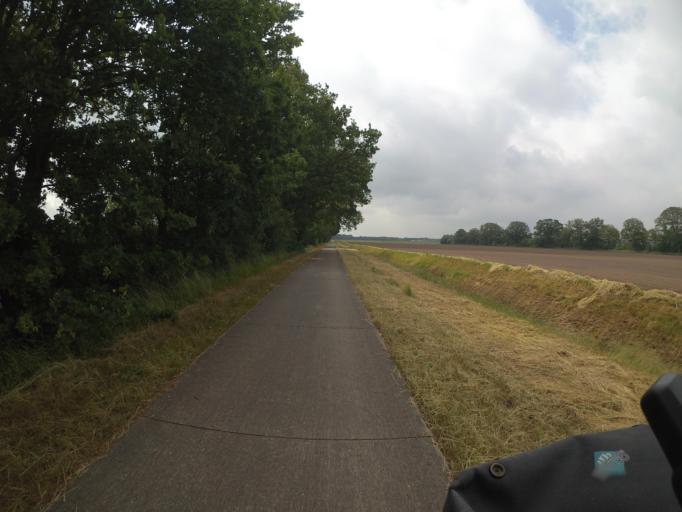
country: NL
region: Drenthe
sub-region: Gemeente Westerveld
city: Havelte
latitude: 52.8458
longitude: 6.2754
